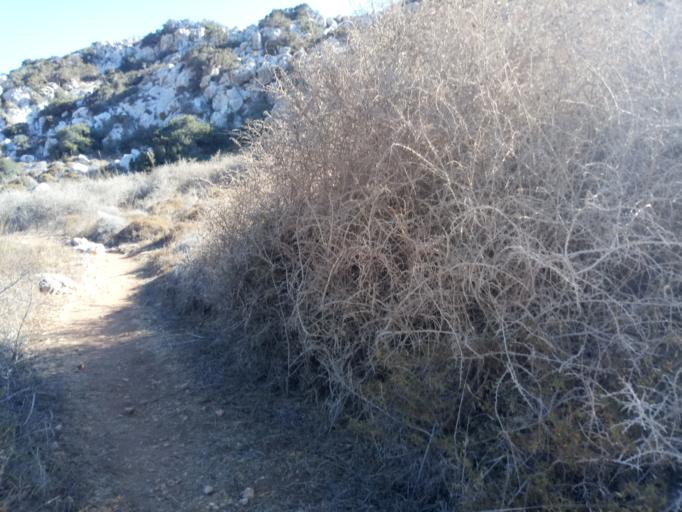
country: CY
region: Ammochostos
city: Protaras
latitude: 34.9658
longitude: 34.0714
